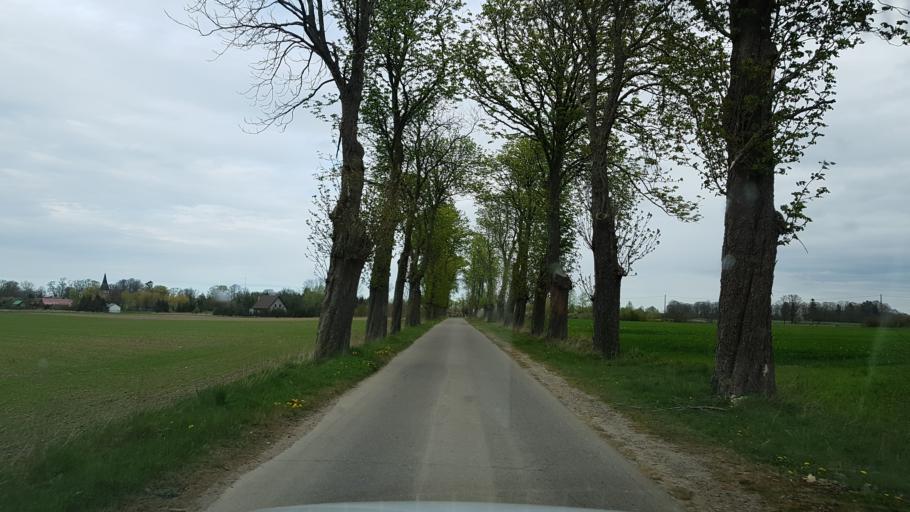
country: PL
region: West Pomeranian Voivodeship
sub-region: Powiat slawienski
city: Slawno
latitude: 54.5139
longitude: 16.6038
